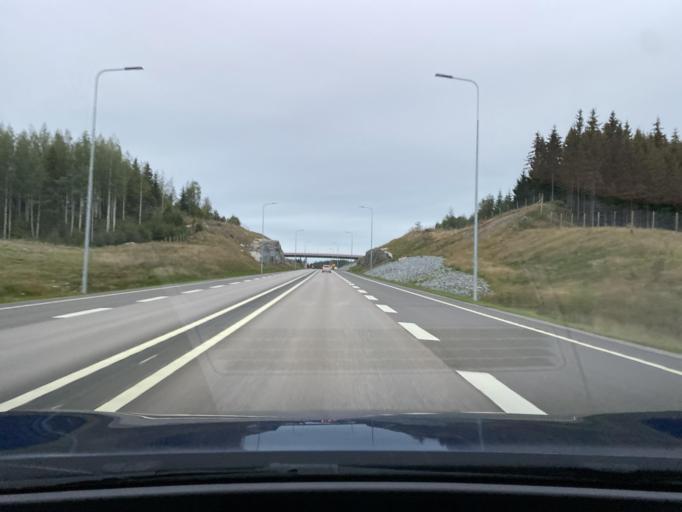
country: FI
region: Paijanne Tavastia
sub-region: Lahti
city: Hollola
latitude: 60.9604
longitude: 25.5370
